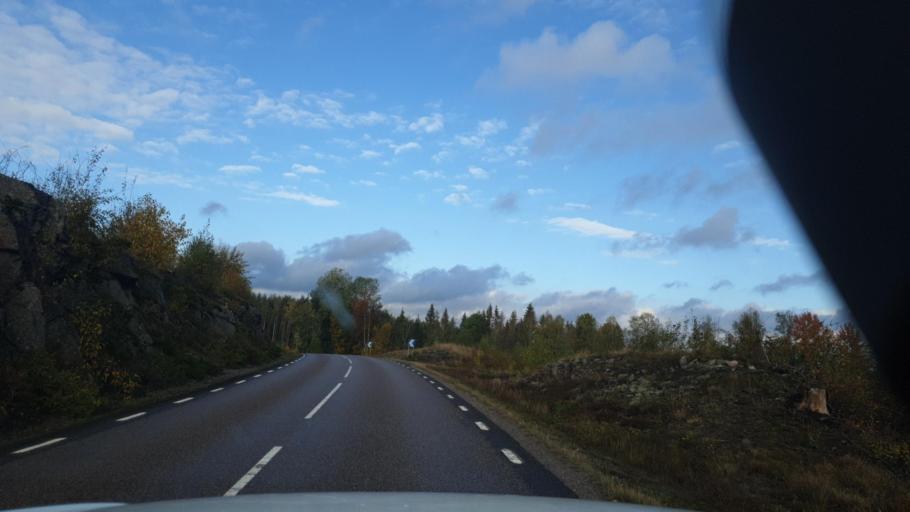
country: SE
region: Vaermland
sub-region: Arvika Kommun
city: Arvika
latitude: 59.4743
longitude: 12.7255
